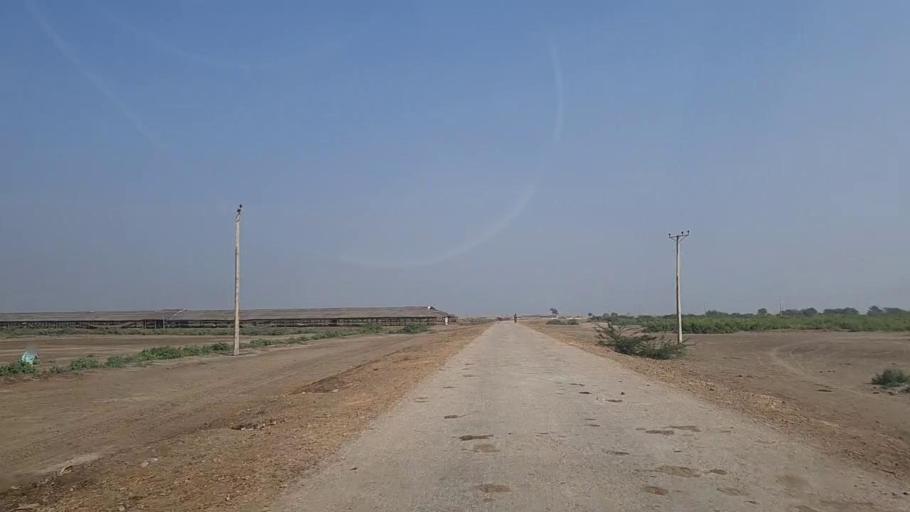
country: PK
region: Sindh
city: Keti Bandar
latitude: 24.2505
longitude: 67.7245
